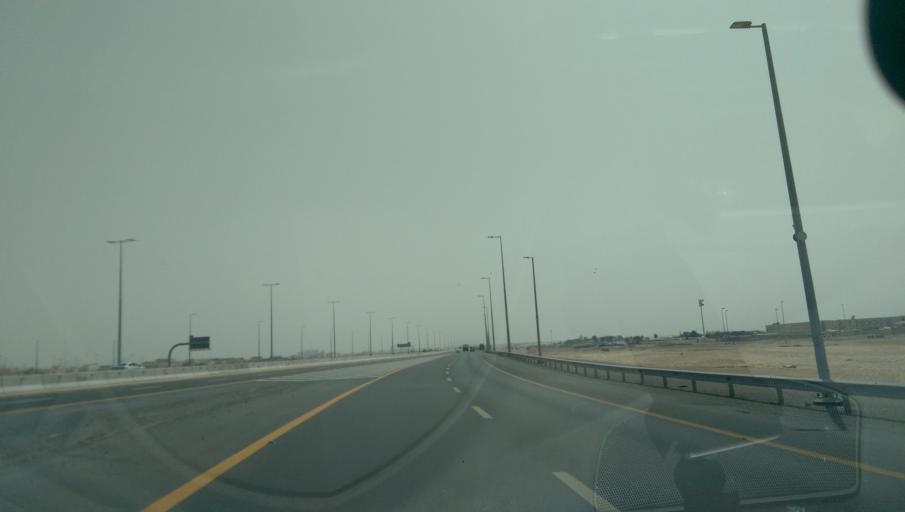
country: AE
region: Abu Dhabi
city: Abu Dhabi
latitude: 24.2905
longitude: 54.5620
